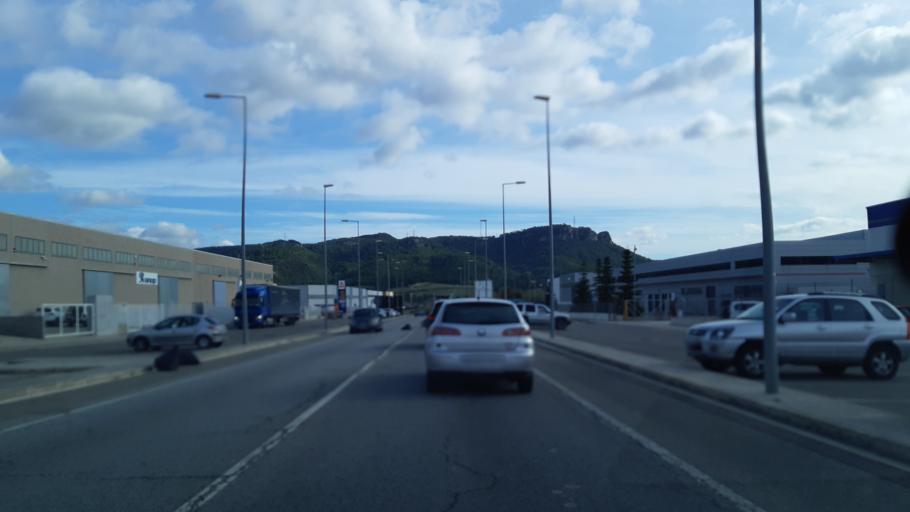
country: ES
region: Catalonia
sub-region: Provincia de Barcelona
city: Vilanova del Cami
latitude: 41.5773
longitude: 1.6549
